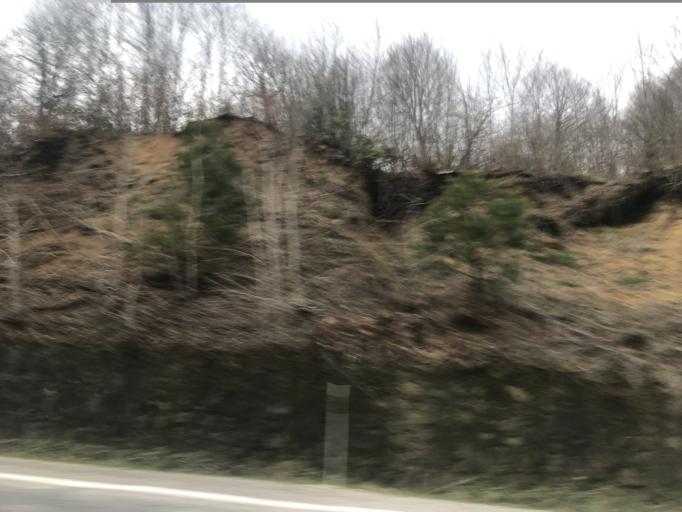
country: TR
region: Bartin
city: Amasra
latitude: 41.7131
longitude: 32.3923
